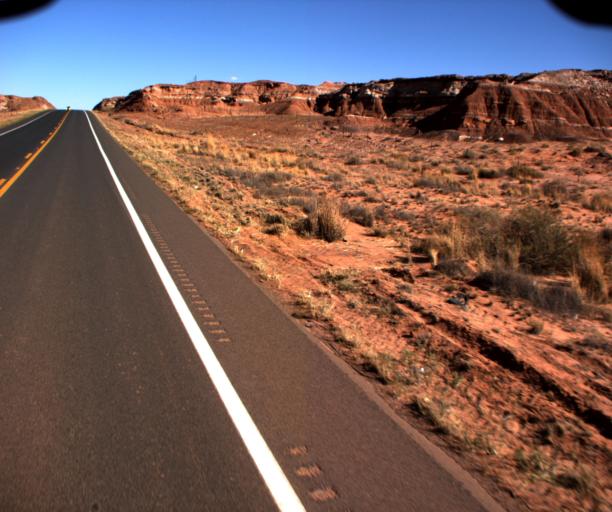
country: US
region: Arizona
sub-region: Coconino County
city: Tuba City
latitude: 36.1023
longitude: -111.2918
